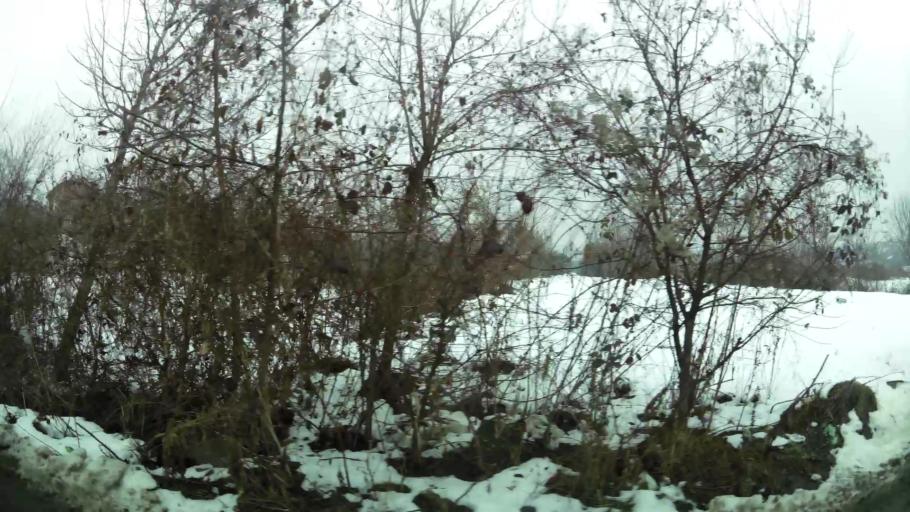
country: RS
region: Central Serbia
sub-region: Belgrade
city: Zvezdara
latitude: 44.7572
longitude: 20.5219
